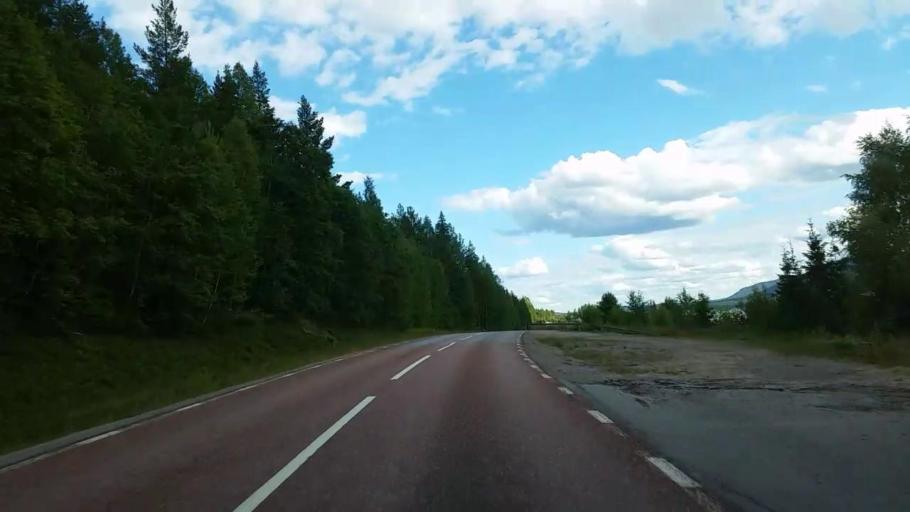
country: SE
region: Gaevleborg
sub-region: Ljusdals Kommun
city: Farila
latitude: 62.1096
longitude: 15.7686
